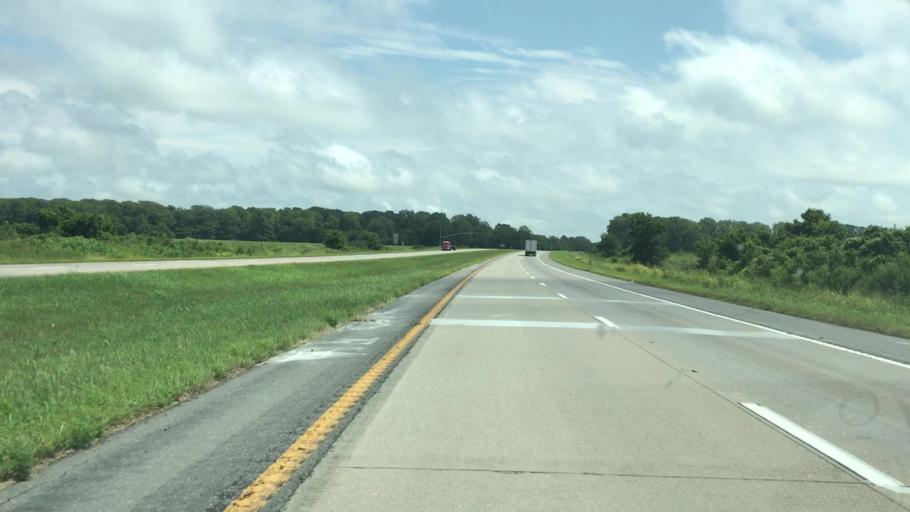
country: US
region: Missouri
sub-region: Pemiscot County
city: Caruthersville
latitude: 36.1386
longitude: -89.6344
